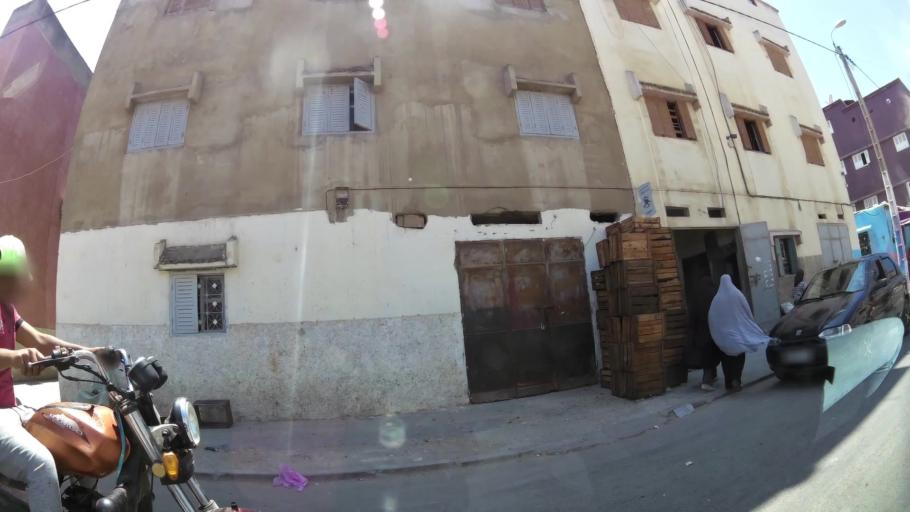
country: MA
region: Gharb-Chrarda-Beni Hssen
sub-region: Kenitra Province
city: Kenitra
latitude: 34.2580
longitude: -6.5539
